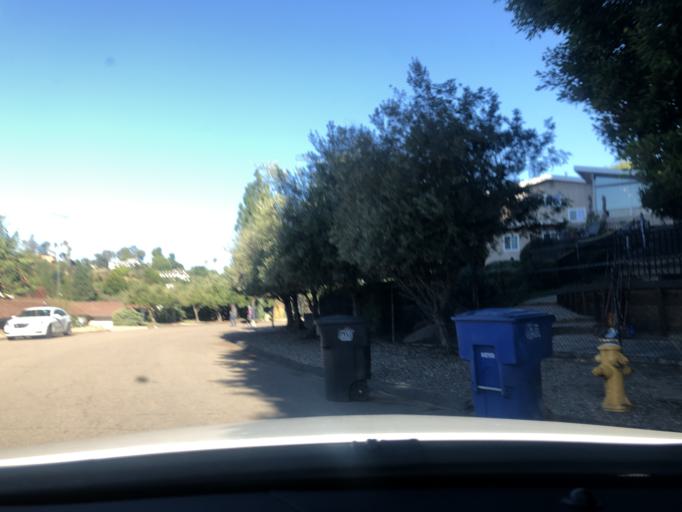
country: US
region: California
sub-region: San Diego County
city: Casa de Oro-Mount Helix
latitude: 32.7670
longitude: -116.9472
